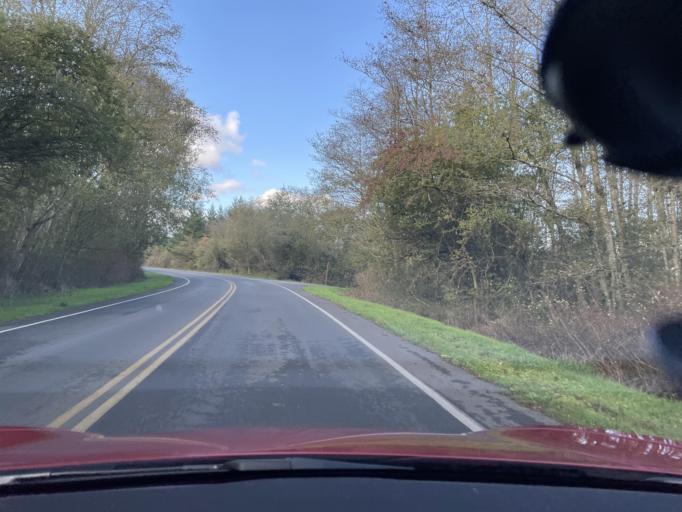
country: US
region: Washington
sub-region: San Juan County
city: Friday Harbor
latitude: 48.4674
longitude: -123.0069
